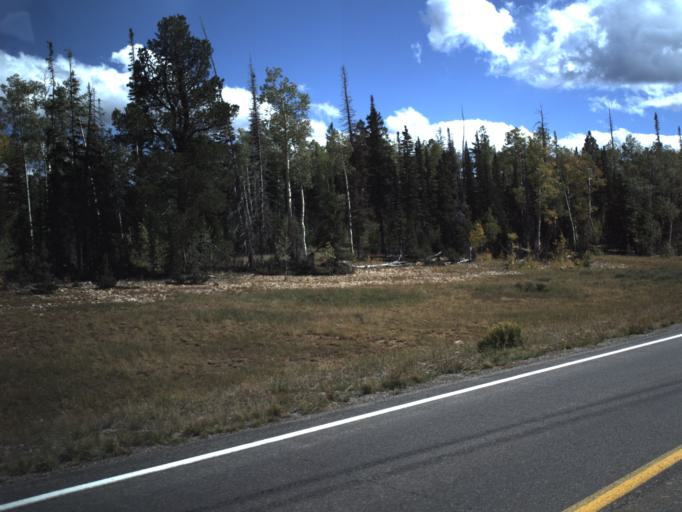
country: US
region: Utah
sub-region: Iron County
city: Parowan
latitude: 37.5492
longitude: -112.7862
